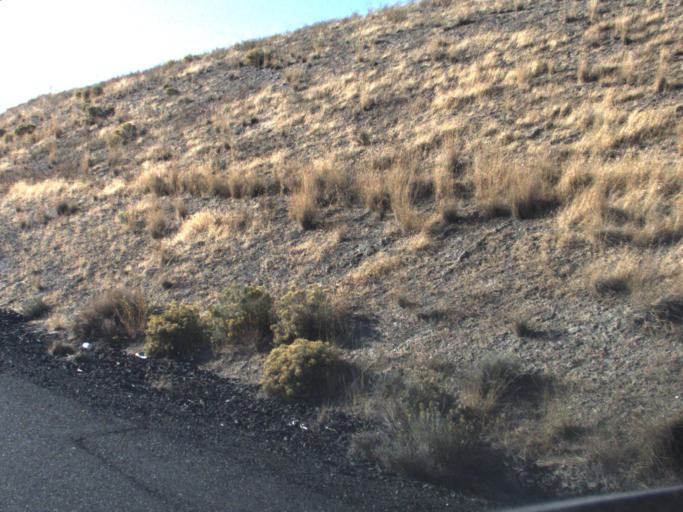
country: US
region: Washington
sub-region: Benton County
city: Finley
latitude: 46.1225
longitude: -119.0455
